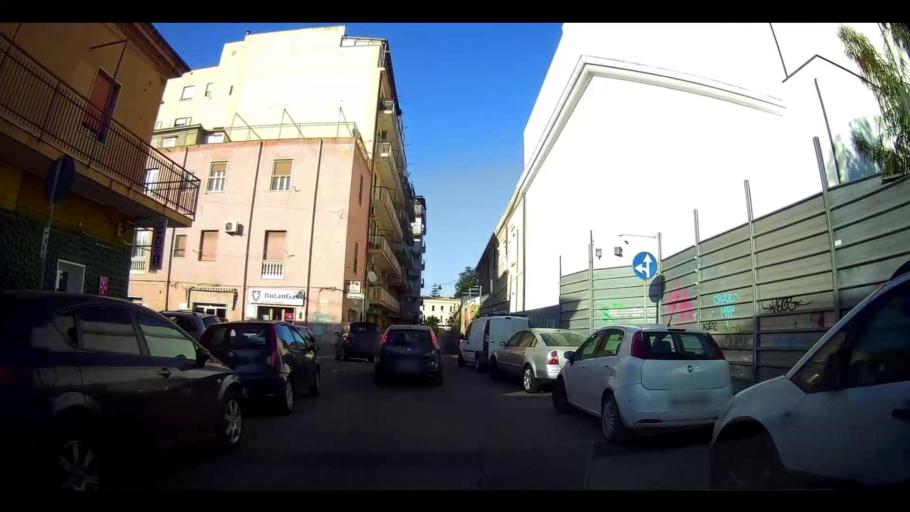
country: IT
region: Calabria
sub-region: Provincia di Crotone
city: Crotone
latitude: 39.0790
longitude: 17.1273
